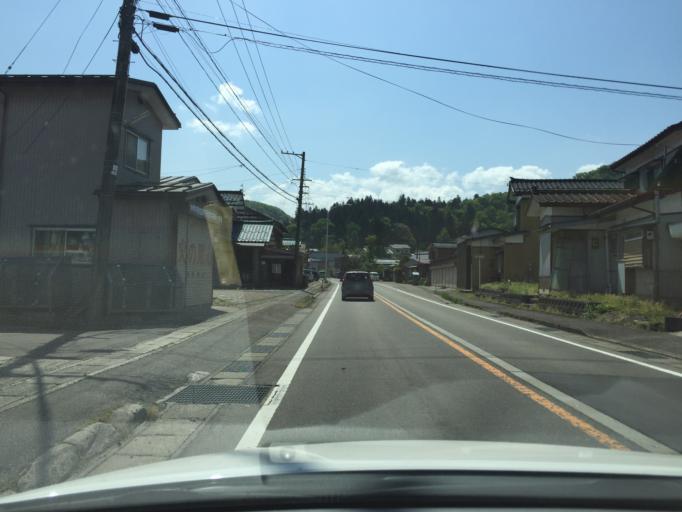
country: JP
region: Niigata
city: Kamo
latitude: 37.6277
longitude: 139.0986
